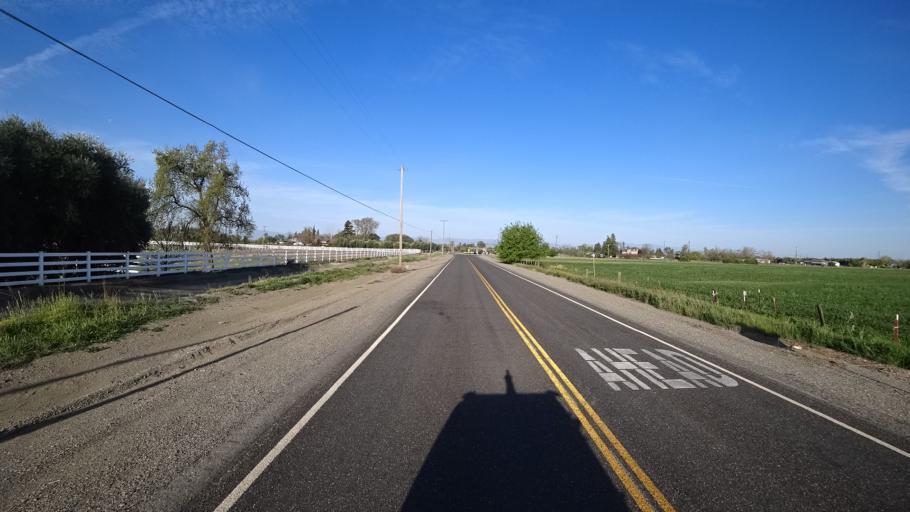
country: US
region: California
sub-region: Glenn County
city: Orland
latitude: 39.7404
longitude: -122.2138
